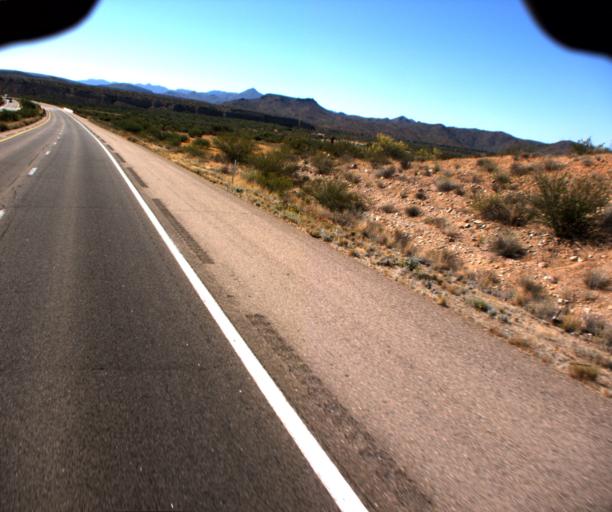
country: US
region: Arizona
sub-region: Yavapai County
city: Bagdad
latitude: 34.6463
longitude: -113.5689
